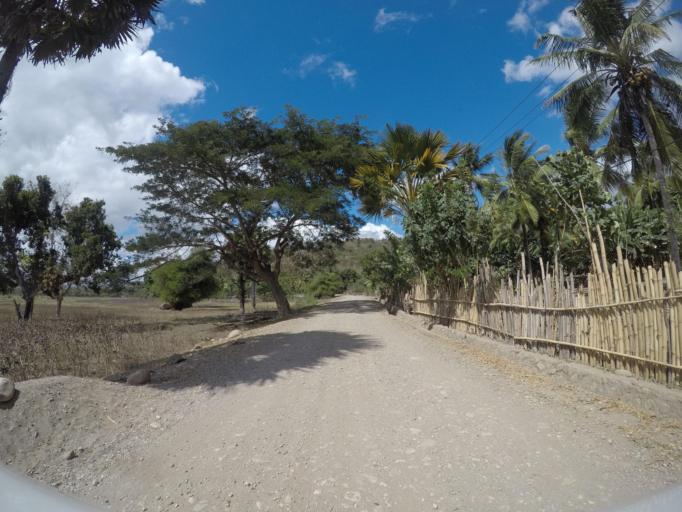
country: TL
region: Lautem
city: Lospalos
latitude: -8.4776
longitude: 126.8165
